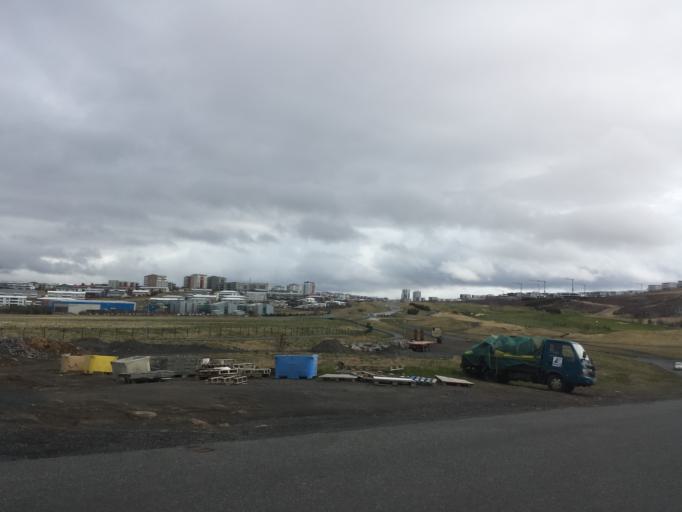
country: IS
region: Capital Region
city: Kopavogur
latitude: 64.0910
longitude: -21.8672
